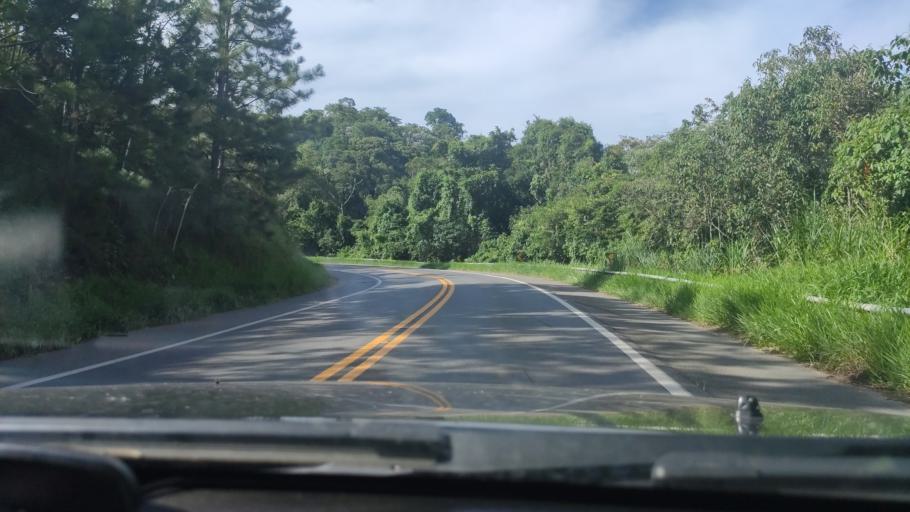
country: BR
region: Sao Paulo
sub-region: Aguas De Lindoia
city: Aguas de Lindoia
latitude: -22.5374
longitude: -46.6286
